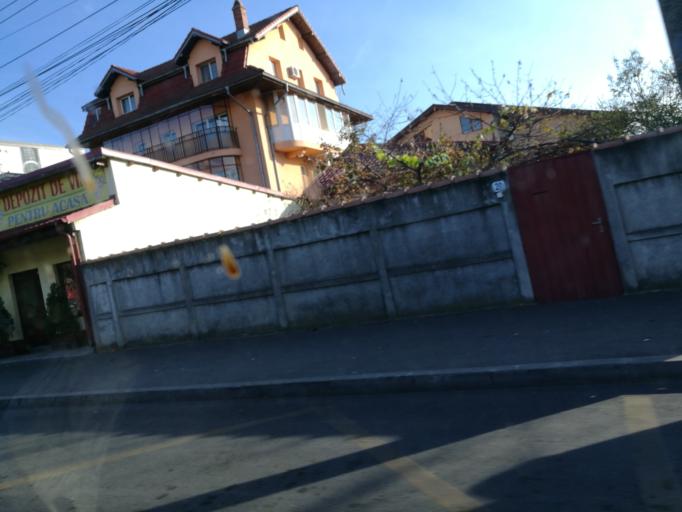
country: RO
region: Ilfov
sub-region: Comuna Chiajna
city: Rosu
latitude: 44.4878
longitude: 26.0499
